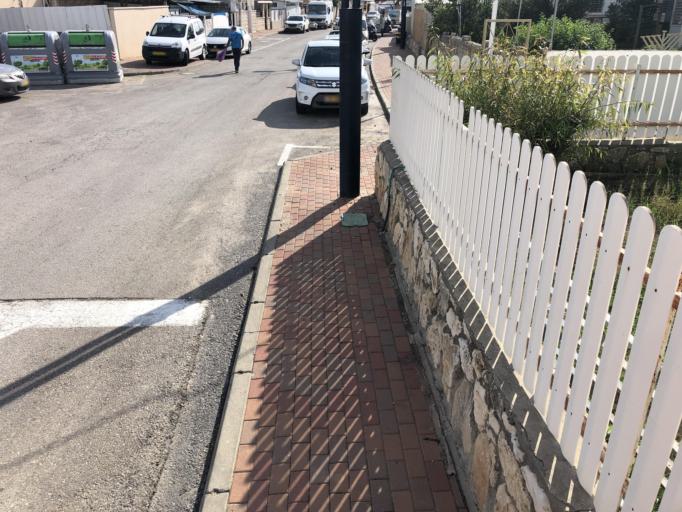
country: IL
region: Northern District
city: `Akko
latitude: 32.9381
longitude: 35.0954
